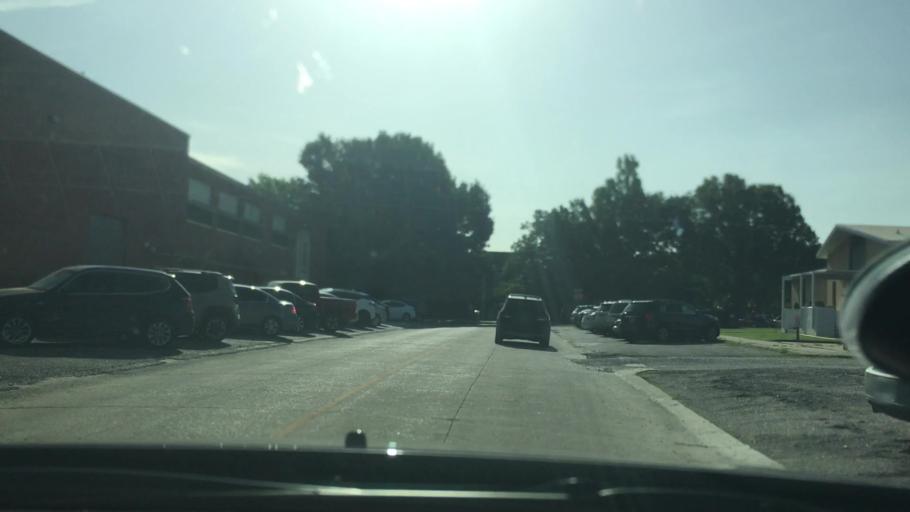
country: US
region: Oklahoma
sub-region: Pontotoc County
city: Ada
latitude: 34.7734
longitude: -96.6665
